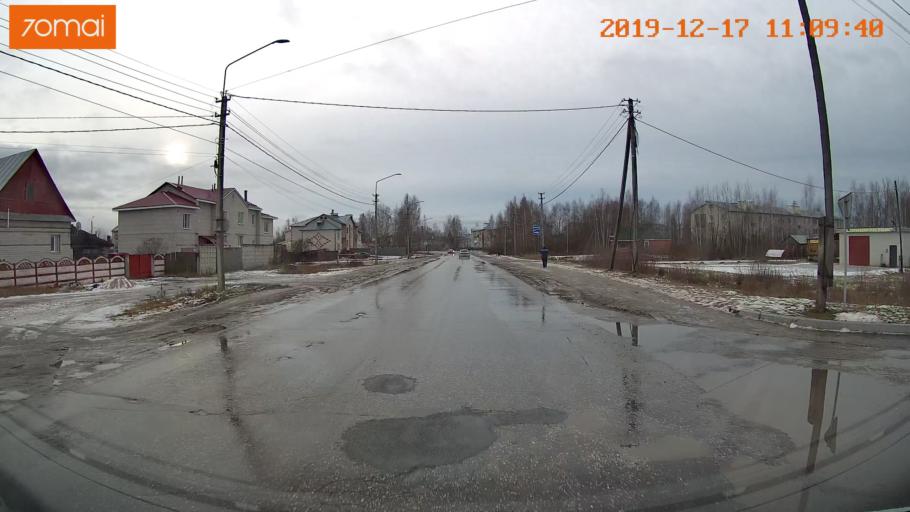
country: RU
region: Vladimir
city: Gus'-Khrustal'nyy
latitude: 55.5987
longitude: 40.6421
